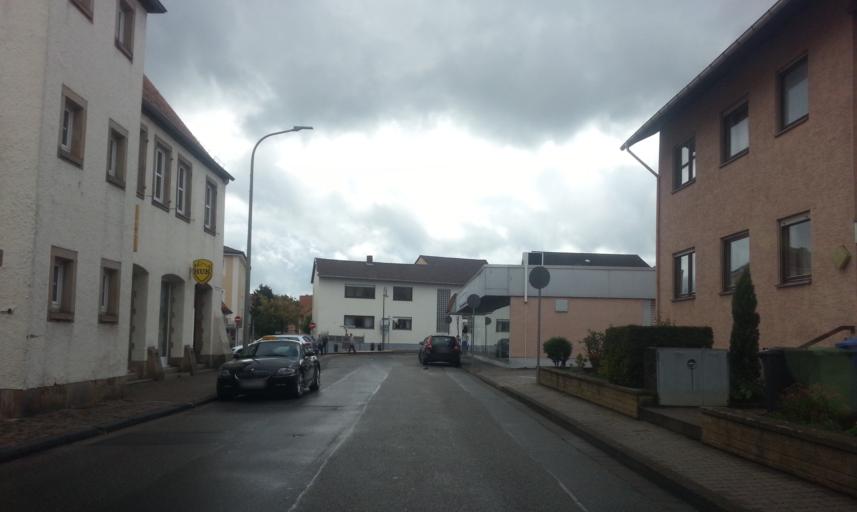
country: DE
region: Rheinland-Pfalz
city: Freinsheim
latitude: 49.5071
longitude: 8.2085
